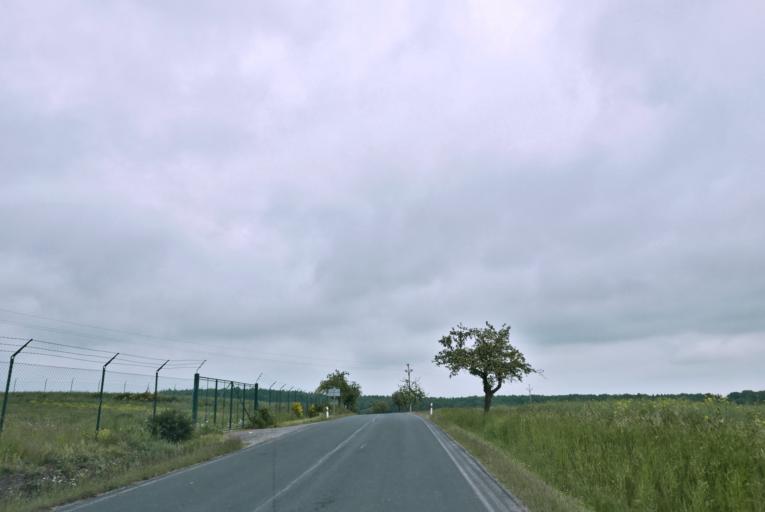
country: CZ
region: Plzensky
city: Plasy
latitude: 49.9854
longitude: 13.4154
